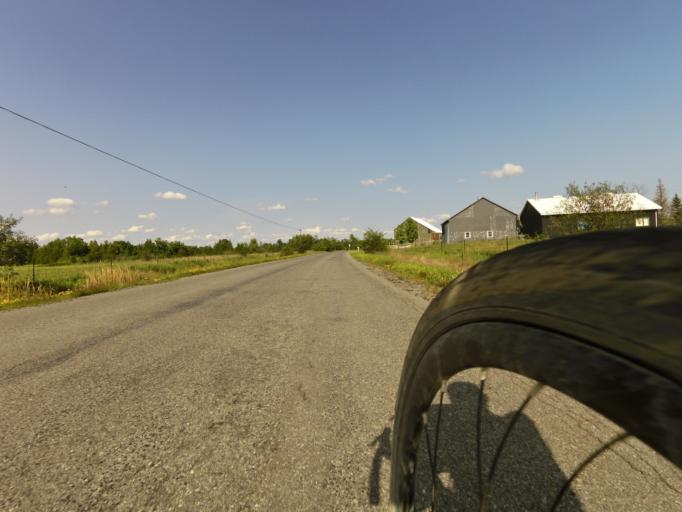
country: CA
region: Ontario
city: Kingston
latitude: 44.3427
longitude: -76.6572
